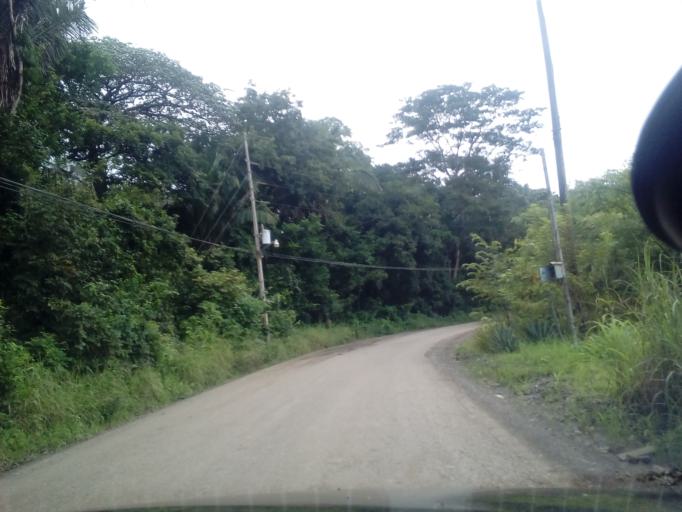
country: CR
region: Guanacaste
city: Samara
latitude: 9.9344
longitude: -85.6495
